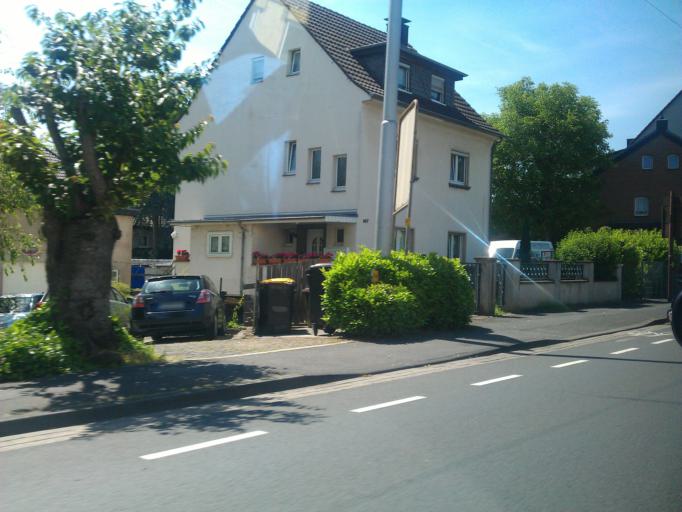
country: DE
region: North Rhine-Westphalia
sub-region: Regierungsbezirk Koln
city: Siegburg
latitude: 50.7878
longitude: 7.2197
